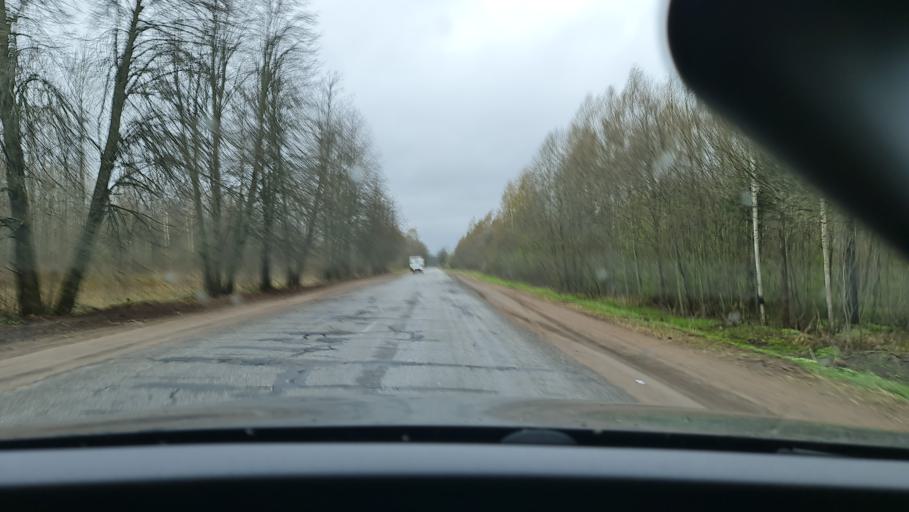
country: RU
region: Novgorod
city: Demyansk
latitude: 57.6690
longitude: 32.5412
